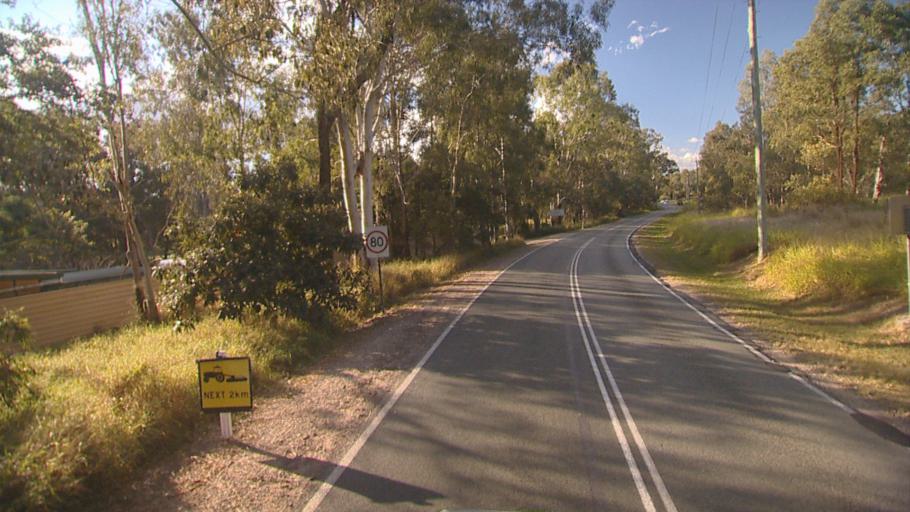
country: AU
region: Queensland
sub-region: Ipswich
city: Springfield Lakes
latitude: -27.7321
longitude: 152.9471
